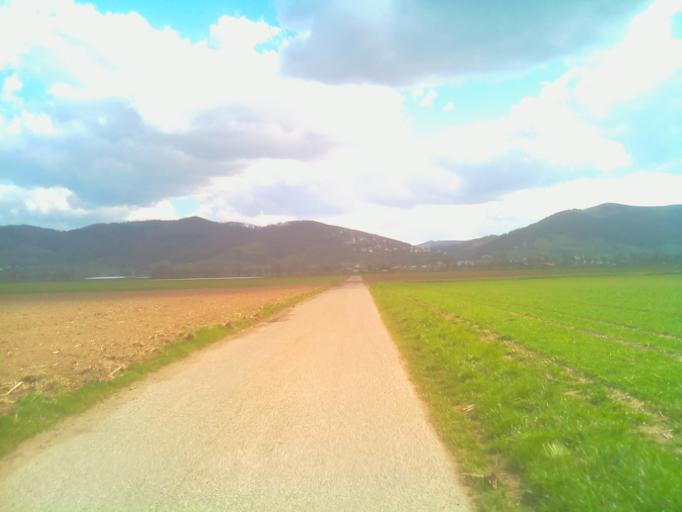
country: DE
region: Baden-Wuerttemberg
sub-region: Karlsruhe Region
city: Ladenburg
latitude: 49.4836
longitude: 8.6326
